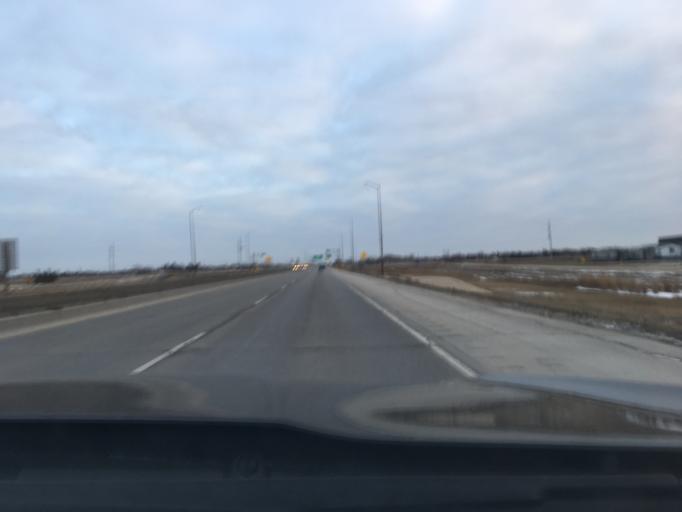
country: CA
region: Manitoba
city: Winnipeg
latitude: 49.9765
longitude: -97.0839
